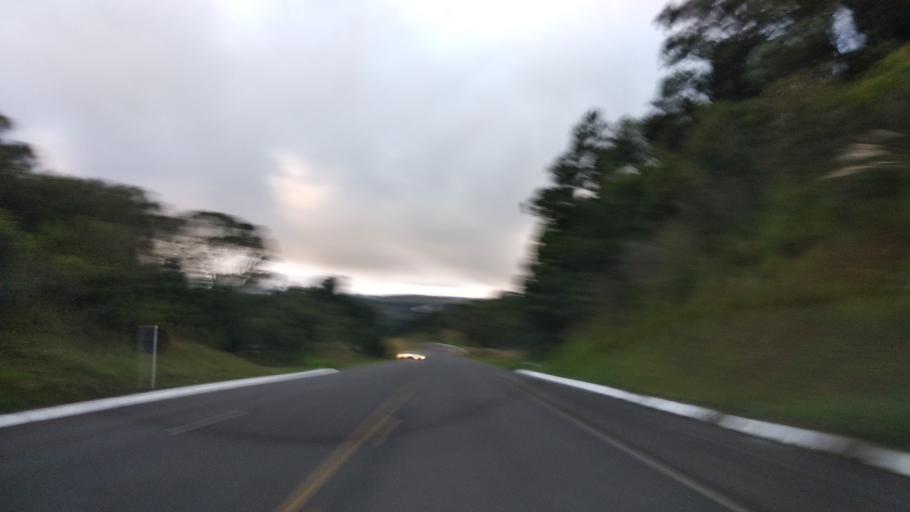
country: BR
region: Santa Catarina
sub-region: Campos Novos
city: Campos Novos
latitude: -27.4445
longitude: -51.0051
